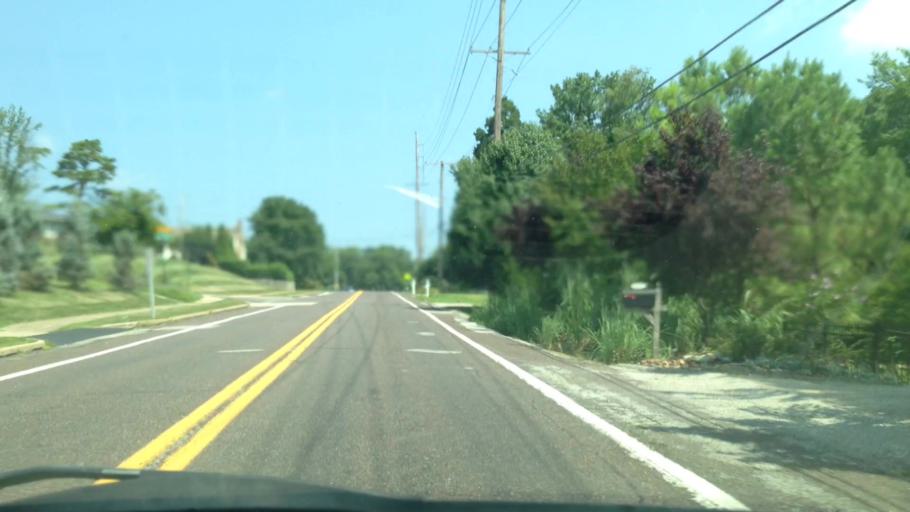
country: US
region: Missouri
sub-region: Saint Louis County
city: Des Peres
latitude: 38.5966
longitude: -90.4441
